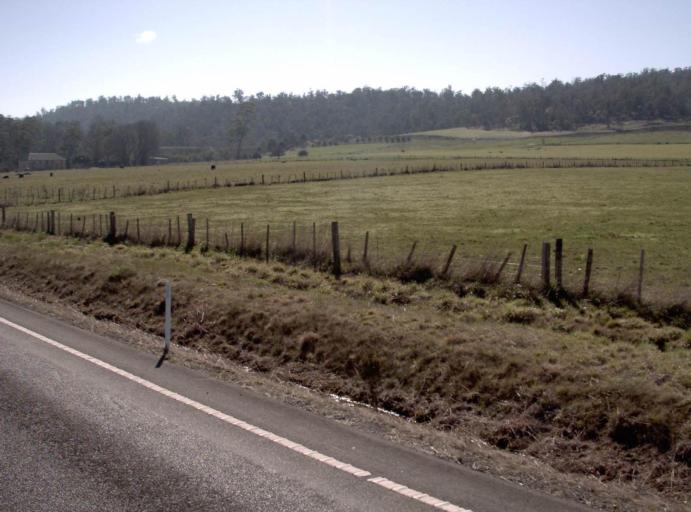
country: AU
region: Tasmania
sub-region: Launceston
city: Mayfield
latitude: -41.3119
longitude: 147.0521
